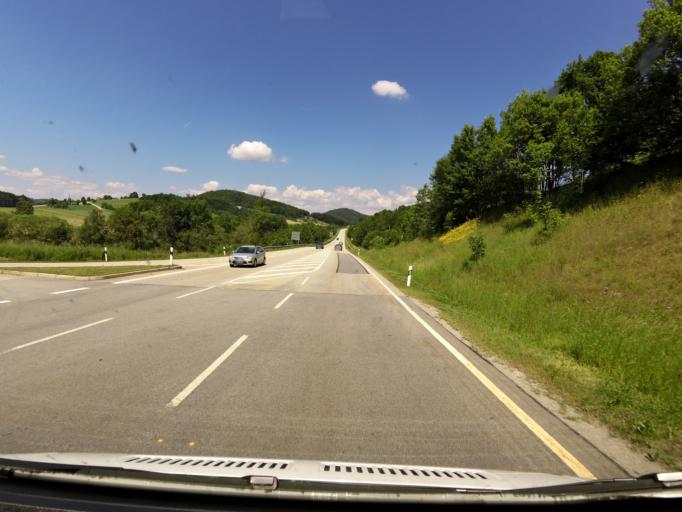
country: DE
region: Bavaria
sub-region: Lower Bavaria
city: Roehrnbach
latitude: 48.7728
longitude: 13.5074
